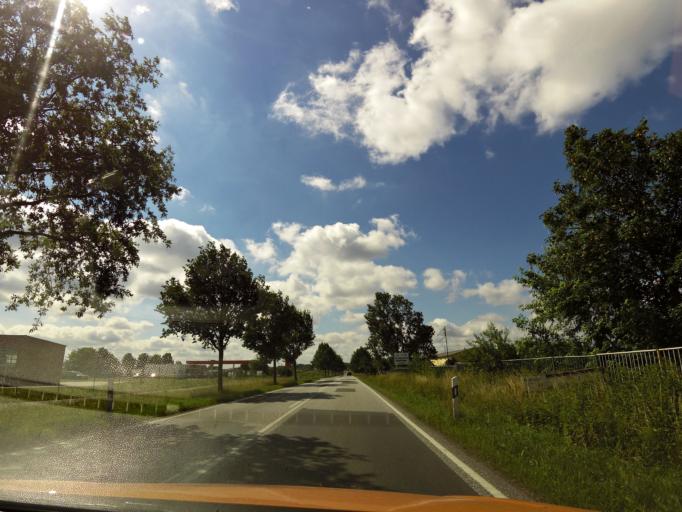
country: DE
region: Mecklenburg-Vorpommern
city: Plau am See
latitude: 53.4715
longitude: 12.2637
